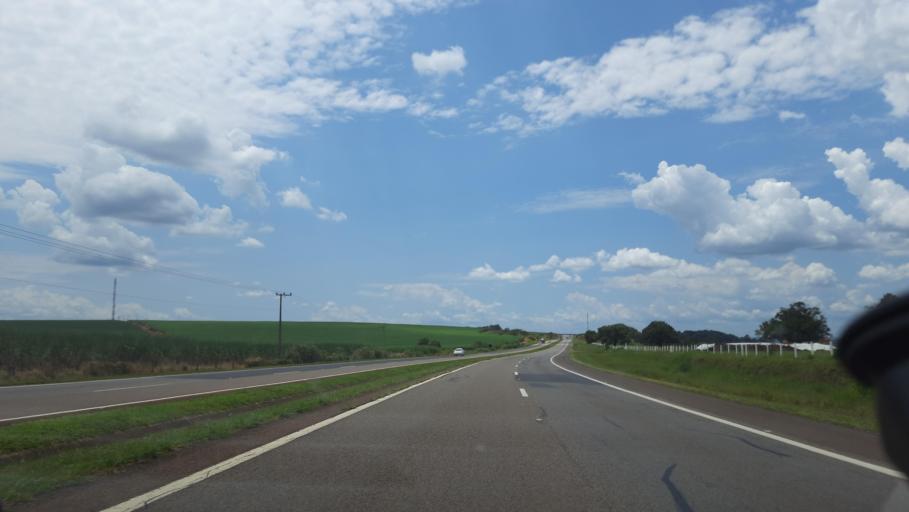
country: BR
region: Sao Paulo
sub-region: Casa Branca
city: Casa Branca
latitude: -21.7019
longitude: -47.0843
